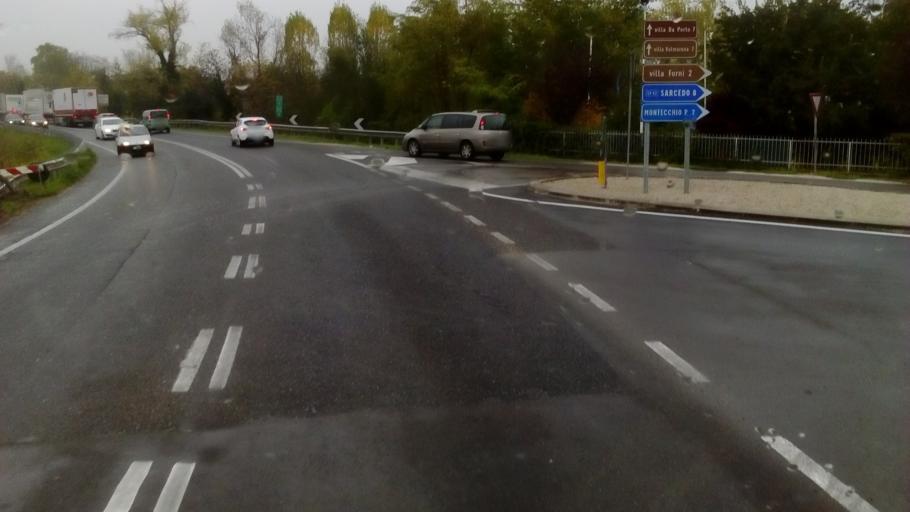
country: IT
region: Veneto
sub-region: Provincia di Vicenza
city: Sandrigo
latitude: 45.6500
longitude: 11.5792
